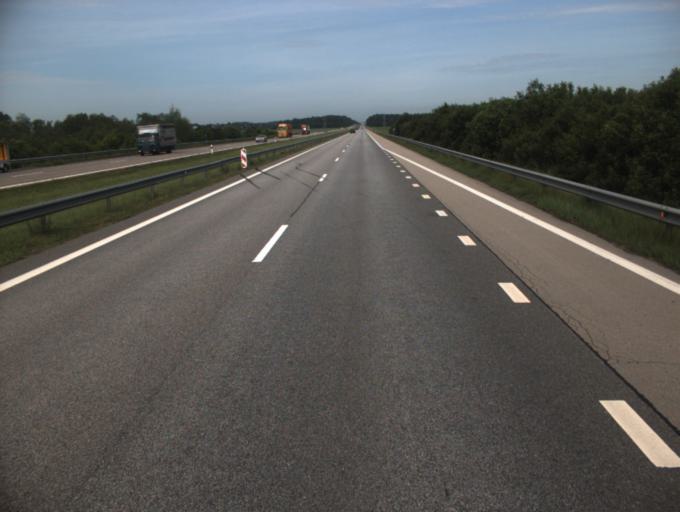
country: LT
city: Raseiniai
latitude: 55.3284
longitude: 23.1418
